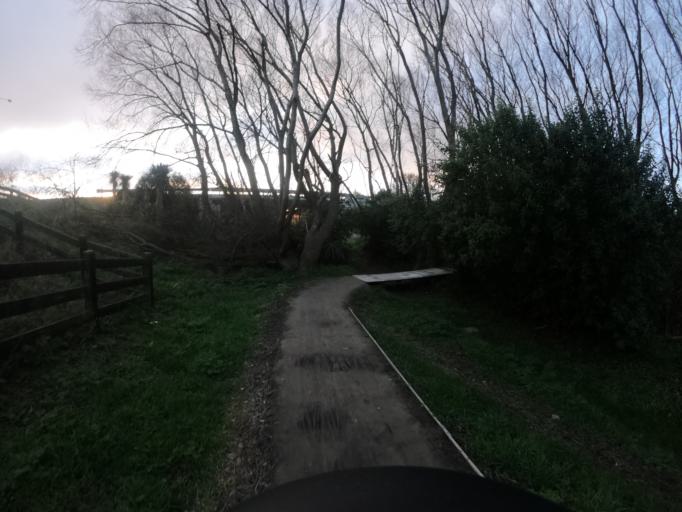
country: NZ
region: Canterbury
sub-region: Selwyn District
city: Prebbleton
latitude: -43.5618
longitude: 172.5617
